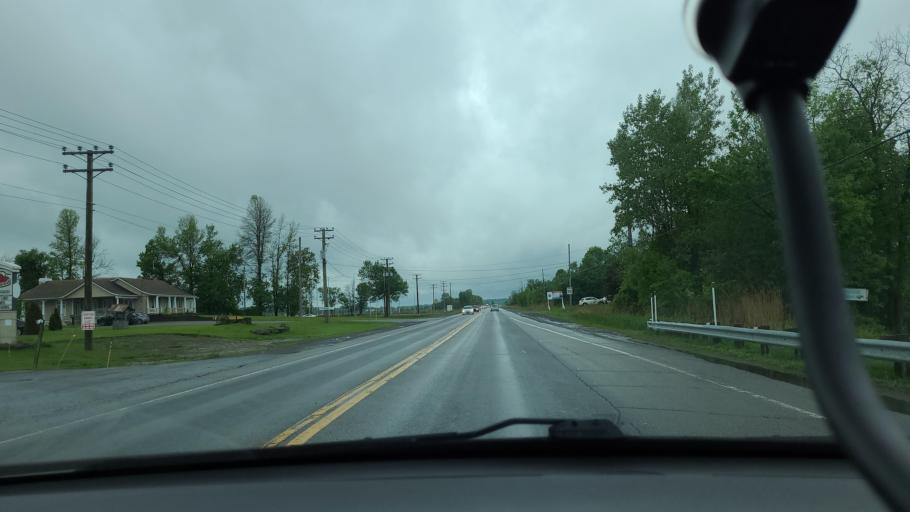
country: CA
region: Quebec
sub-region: Laurentides
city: Saint-Jerome
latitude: 45.7338
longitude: -74.0469
